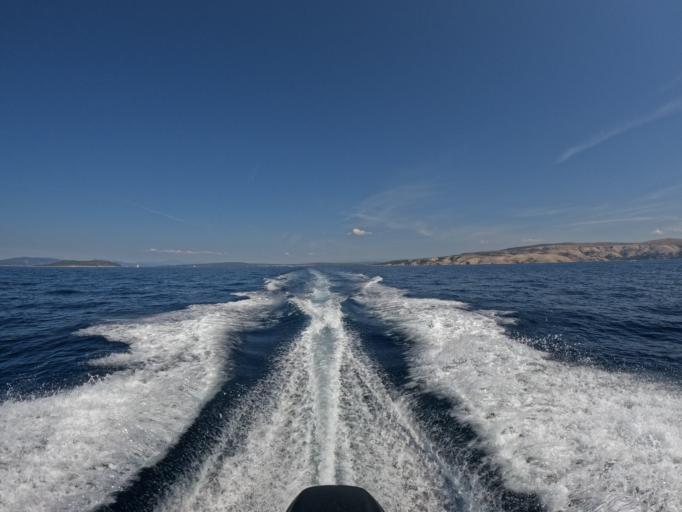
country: HR
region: Primorsko-Goranska
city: Punat
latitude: 44.9254
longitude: 14.6199
